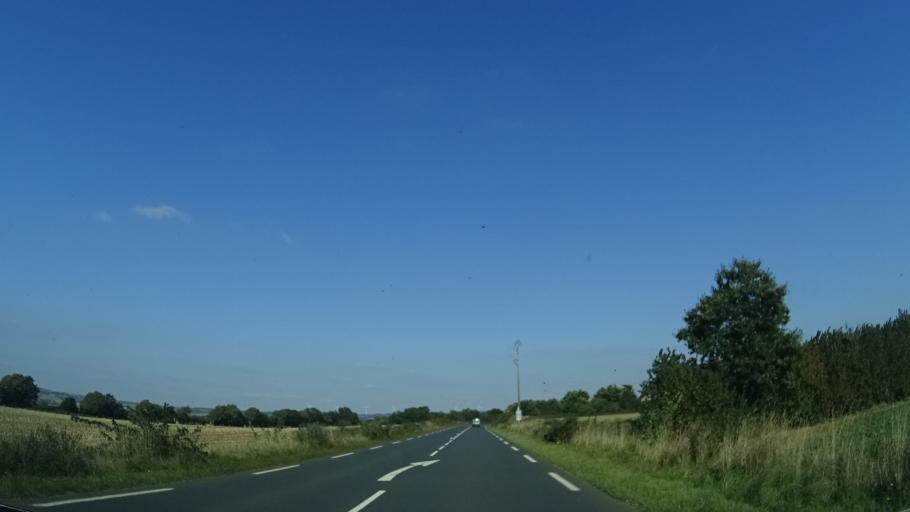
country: FR
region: Brittany
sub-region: Departement du Finistere
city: Plonevez-Porzay
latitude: 48.1364
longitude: -4.1840
